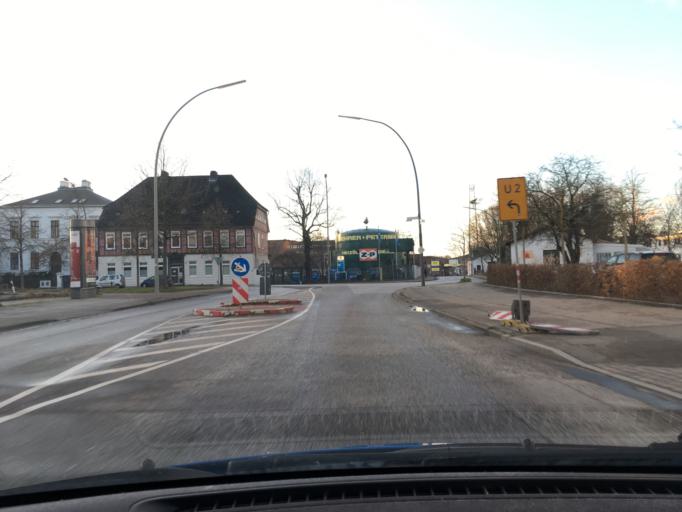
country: DE
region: Hamburg
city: Harburg
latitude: 53.4665
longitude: 9.9848
